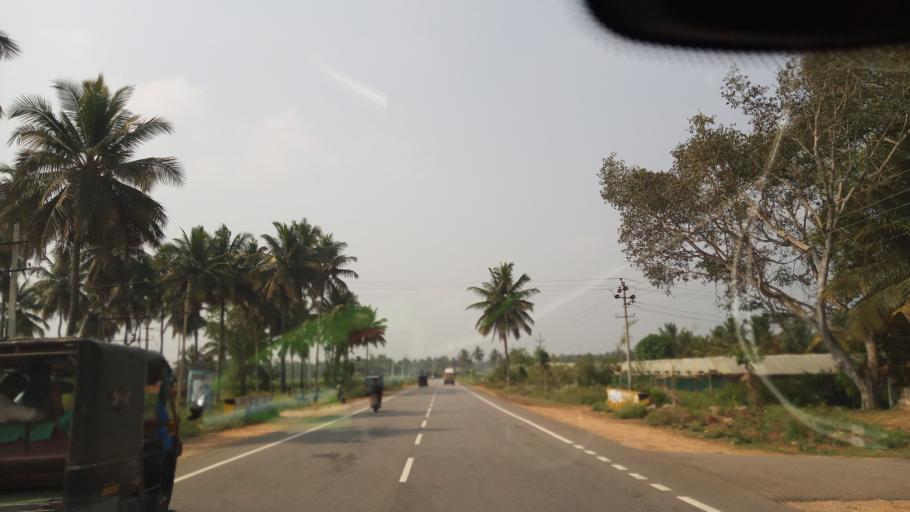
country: IN
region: Karnataka
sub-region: Mandya
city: Pandavapura
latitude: 12.5464
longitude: 76.6712
